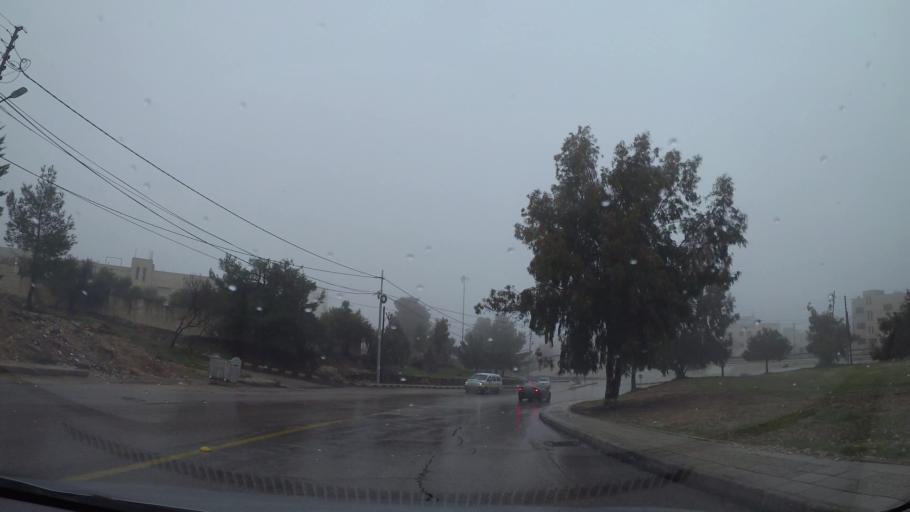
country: JO
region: Amman
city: Al Jubayhah
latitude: 32.0283
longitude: 35.8272
